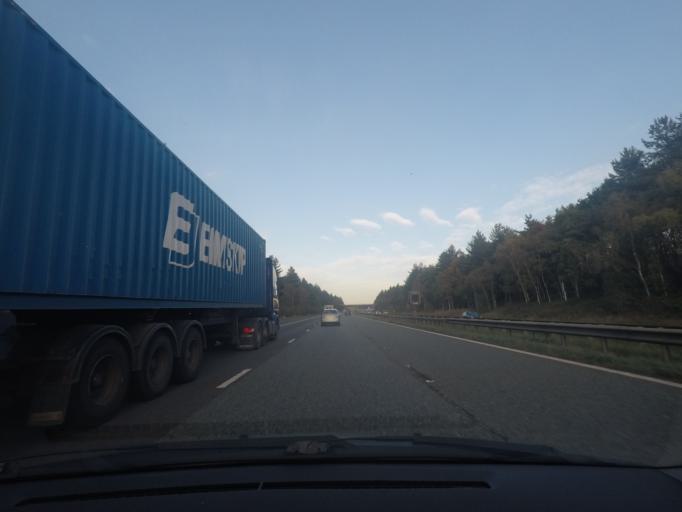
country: GB
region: England
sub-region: North Lincolnshire
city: Worlaby
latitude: 53.5728
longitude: -0.4691
